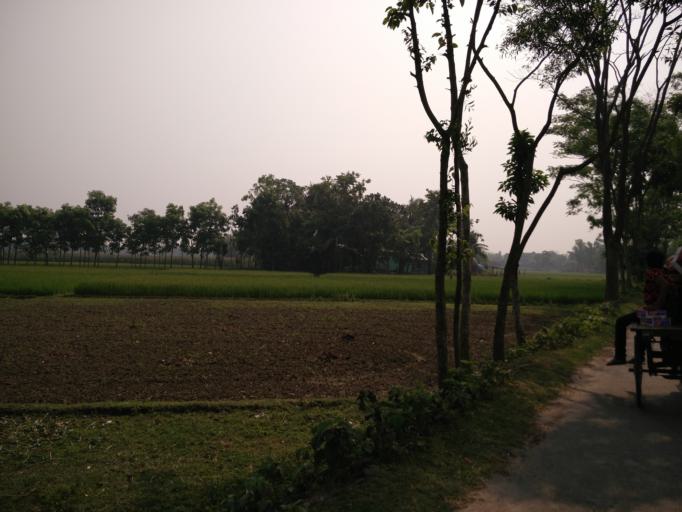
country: BD
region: Dhaka
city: Muktagacha
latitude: 24.9147
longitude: 90.2243
